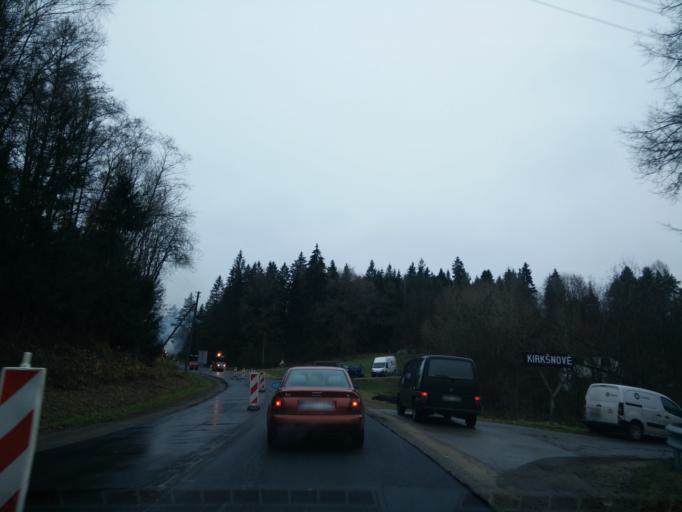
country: LT
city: Ariogala
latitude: 55.3015
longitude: 23.4389
